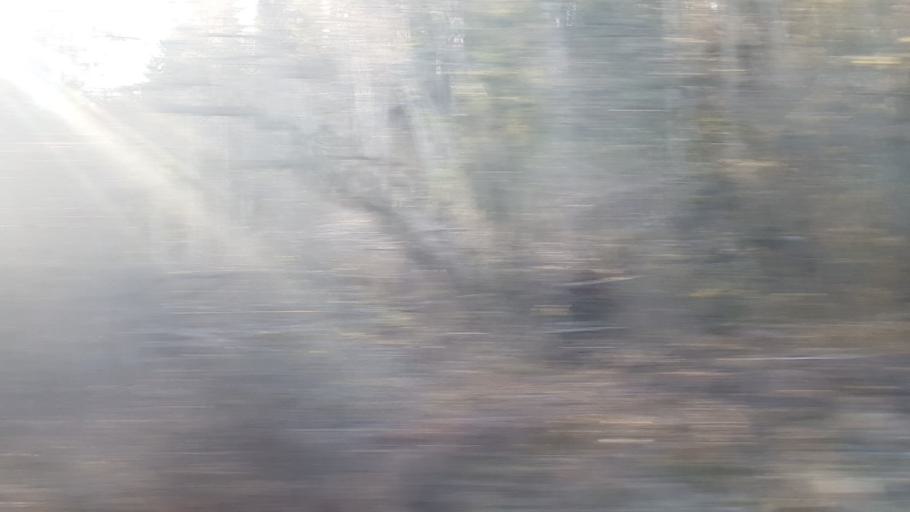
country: NO
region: Nord-Trondelag
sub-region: Levanger
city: Levanger
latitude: 63.7239
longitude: 11.2657
